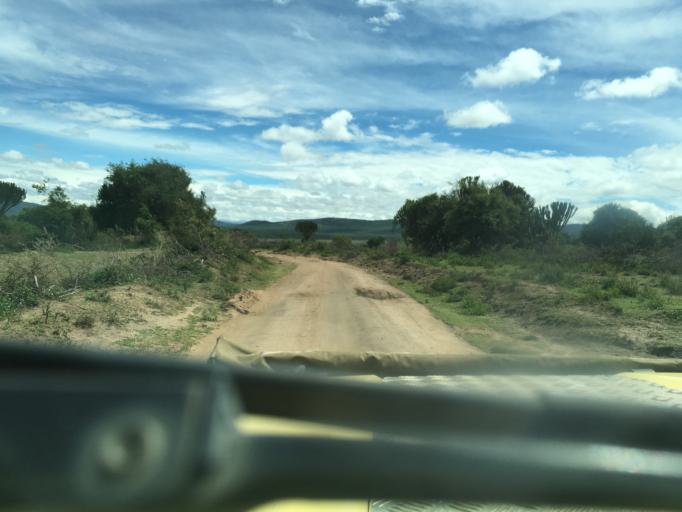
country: TZ
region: Mara
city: Mugumu
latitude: -1.8904
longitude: 35.3635
